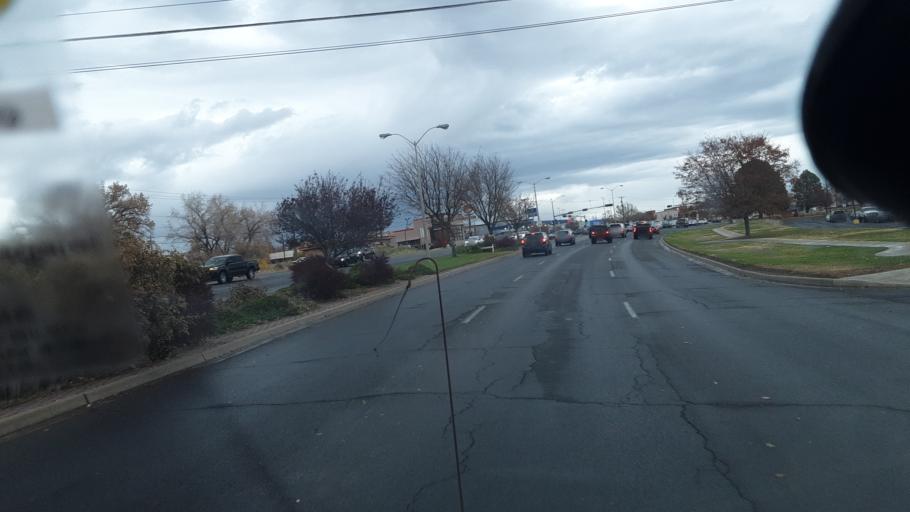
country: US
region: New Mexico
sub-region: San Juan County
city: Farmington
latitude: 36.7625
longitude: -108.1550
